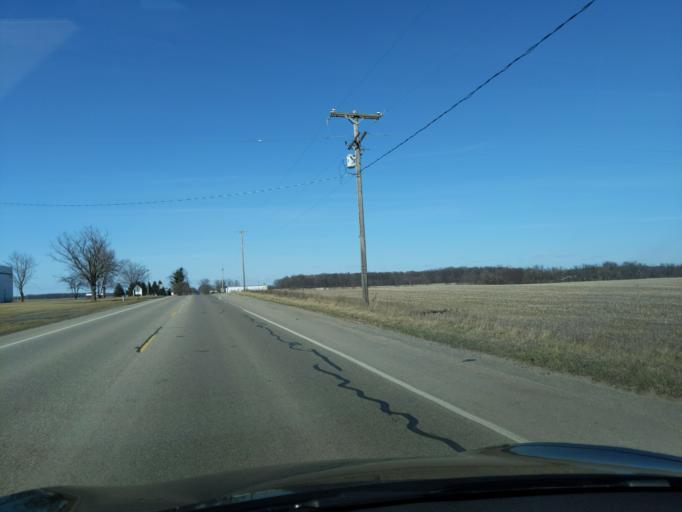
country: US
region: Michigan
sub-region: Ionia County
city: Lake Odessa
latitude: 42.7929
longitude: -85.1333
